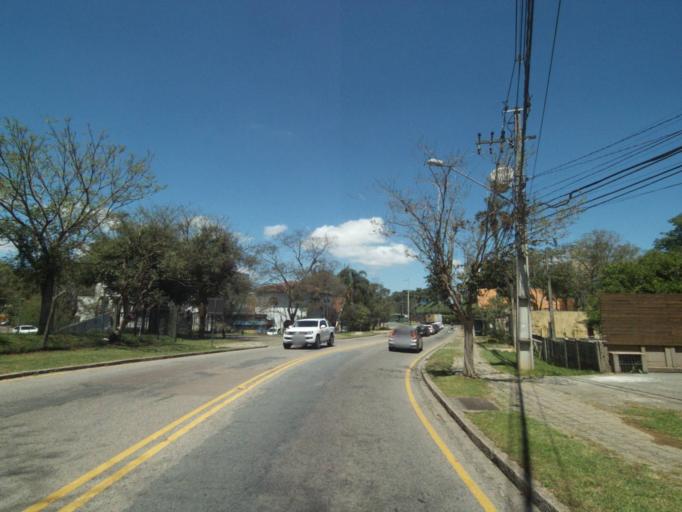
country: BR
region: Parana
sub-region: Curitiba
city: Curitiba
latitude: -25.3867
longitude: -49.2674
